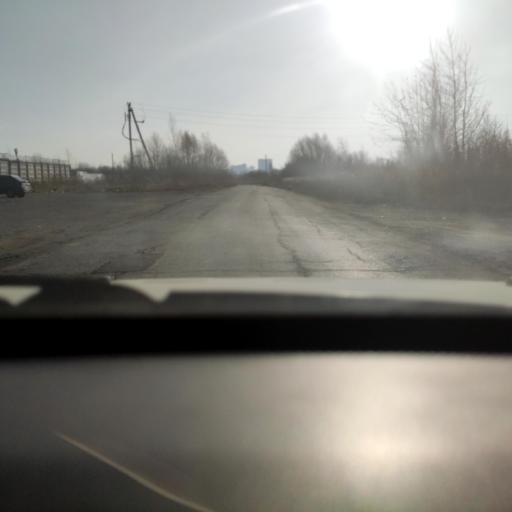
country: RU
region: Perm
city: Perm
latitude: 58.0361
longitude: 56.1907
